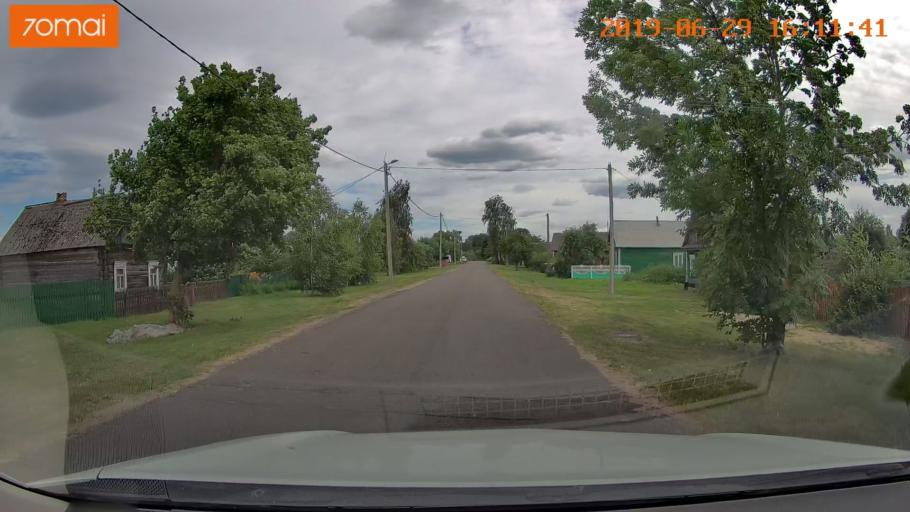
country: BY
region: Brest
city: Luninyets
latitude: 52.2035
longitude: 27.0119
